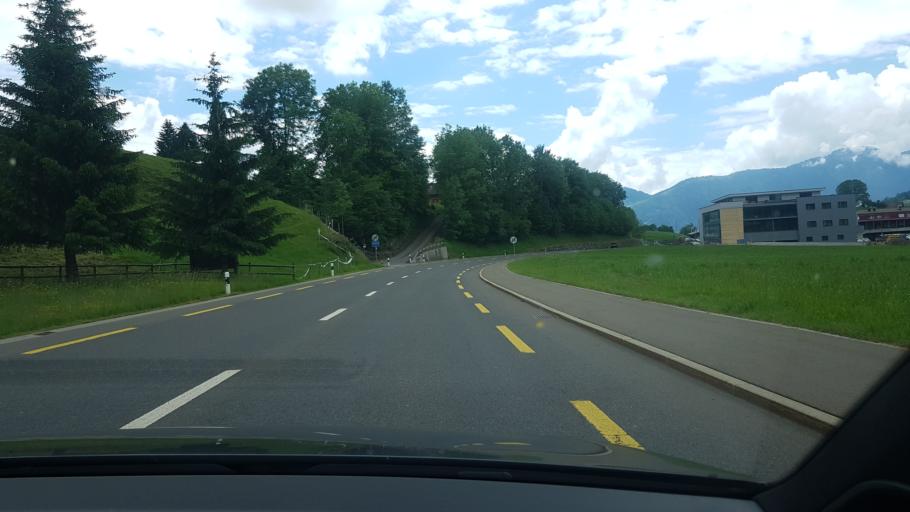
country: CH
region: Schwyz
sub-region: Bezirk Schwyz
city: Sattel
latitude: 47.0759
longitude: 8.6314
